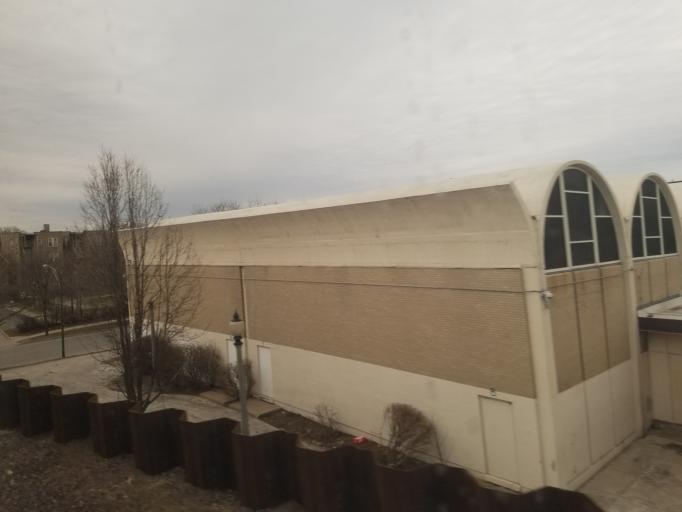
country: US
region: Illinois
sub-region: Cook County
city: Cicero
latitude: 41.8515
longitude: -87.7149
